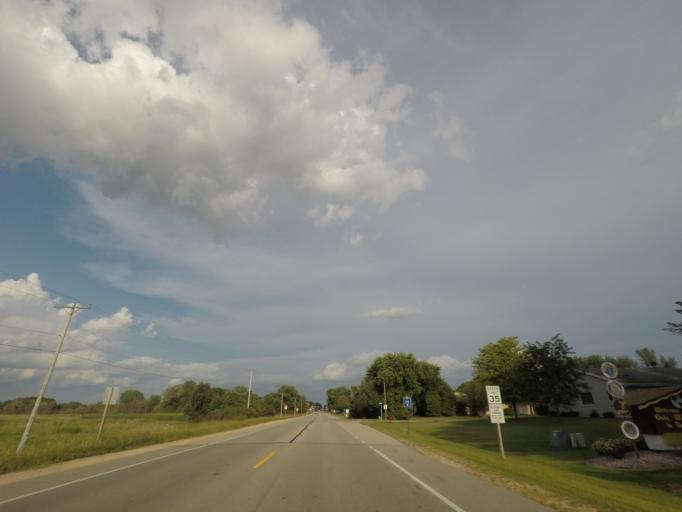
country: US
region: Wisconsin
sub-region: Dane County
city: Waunakee
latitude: 43.1921
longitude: -89.4715
